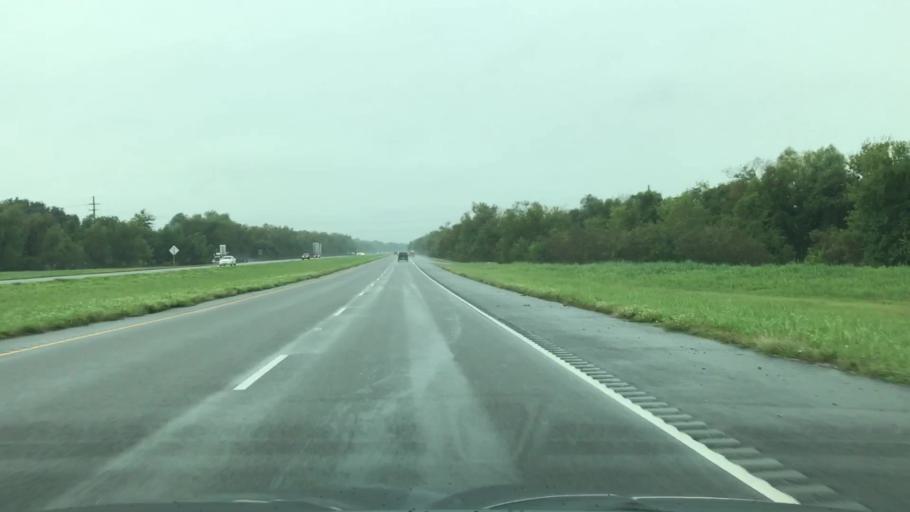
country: US
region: Louisiana
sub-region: Lafourche Parish
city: Raceland
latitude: 29.7052
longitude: -90.5747
